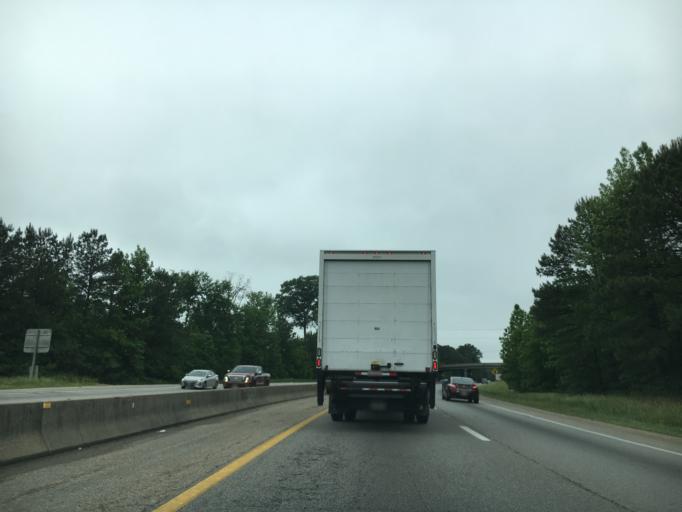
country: US
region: Virginia
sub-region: City of Petersburg
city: Petersburg
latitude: 37.1995
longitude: -77.4277
